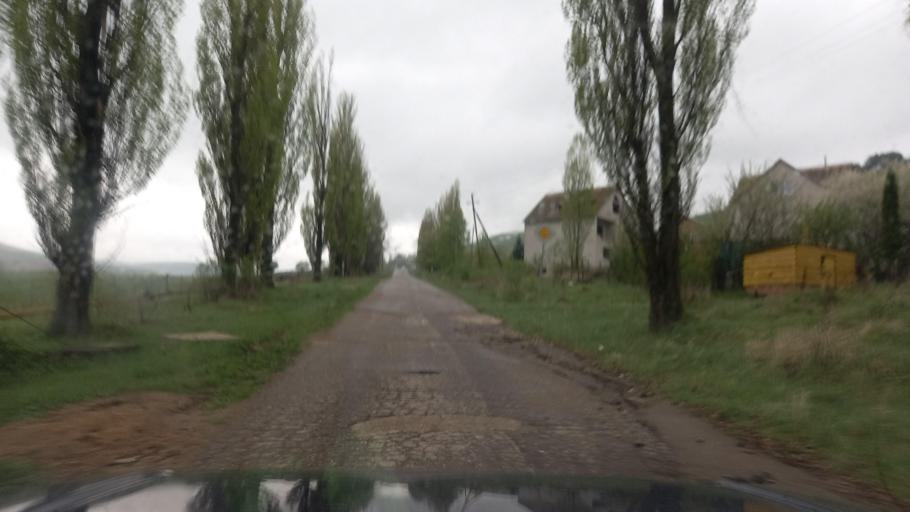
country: RU
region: Stavropol'skiy
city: Nezhinskiy
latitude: 43.8759
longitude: 42.6751
